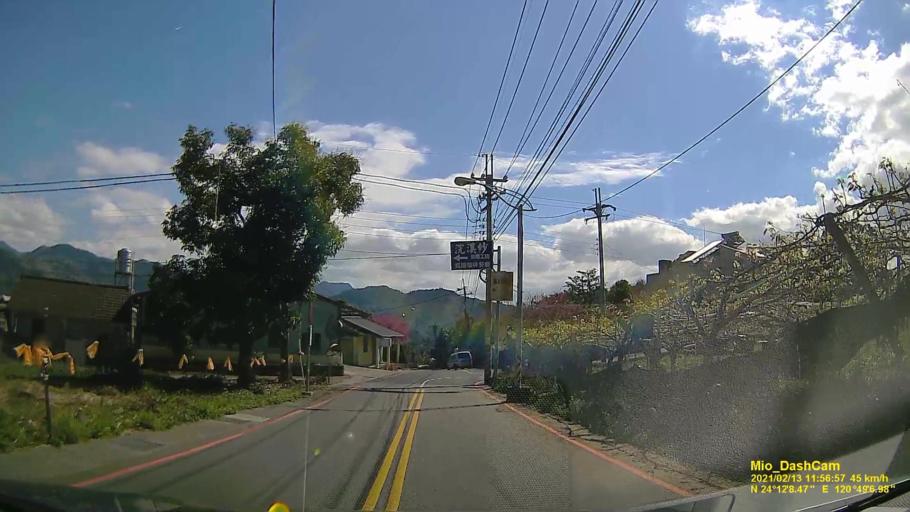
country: TW
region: Taiwan
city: Fengyuan
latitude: 24.2023
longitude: 120.8187
